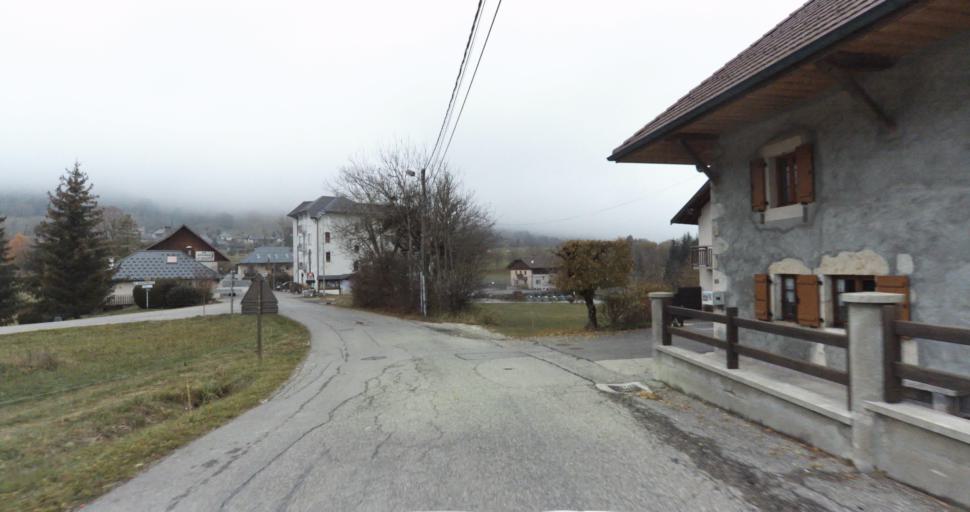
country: FR
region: Rhone-Alpes
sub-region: Departement de la Haute-Savoie
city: Saint-Jorioz
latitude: 45.7713
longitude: 6.1331
